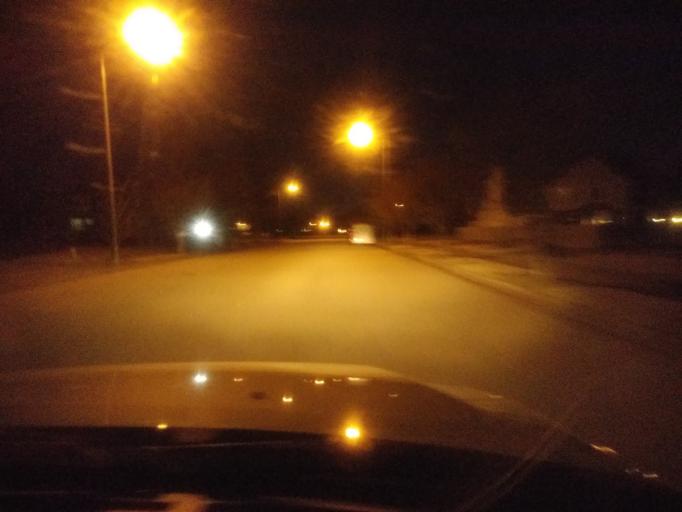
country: US
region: Virginia
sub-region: City of Chesapeake
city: Chesapeake
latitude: 36.7559
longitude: -76.2094
